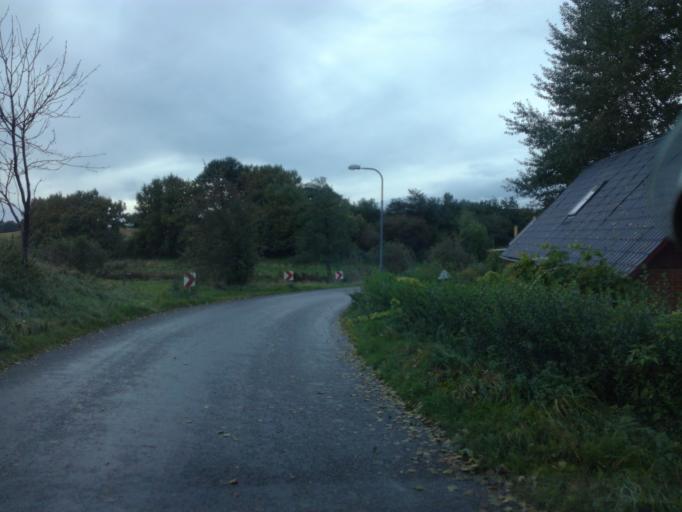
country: DK
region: South Denmark
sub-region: Fredericia Kommune
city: Fredericia
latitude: 55.6083
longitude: 9.7266
